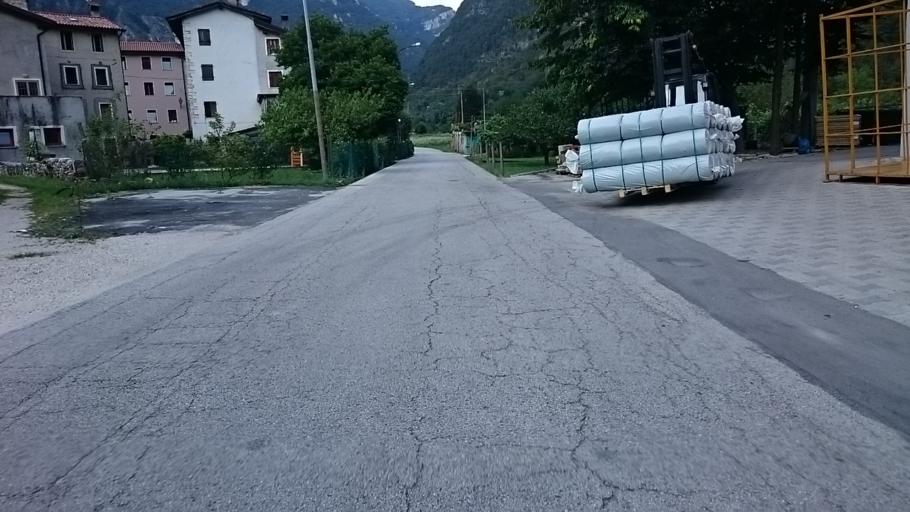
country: IT
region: Veneto
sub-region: Provincia di Vicenza
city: Valstagna
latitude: 45.8892
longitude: 11.6866
